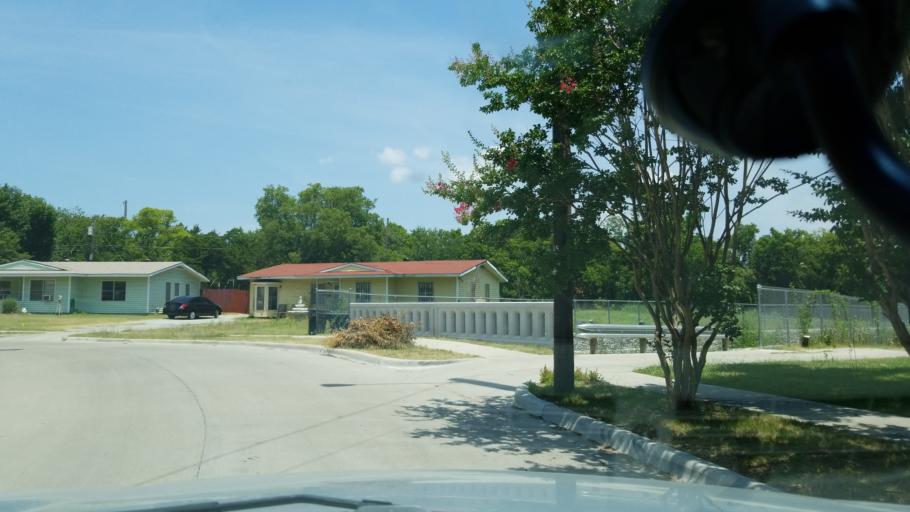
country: US
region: Texas
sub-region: Dallas County
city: Cockrell Hill
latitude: 32.7229
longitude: -96.8590
